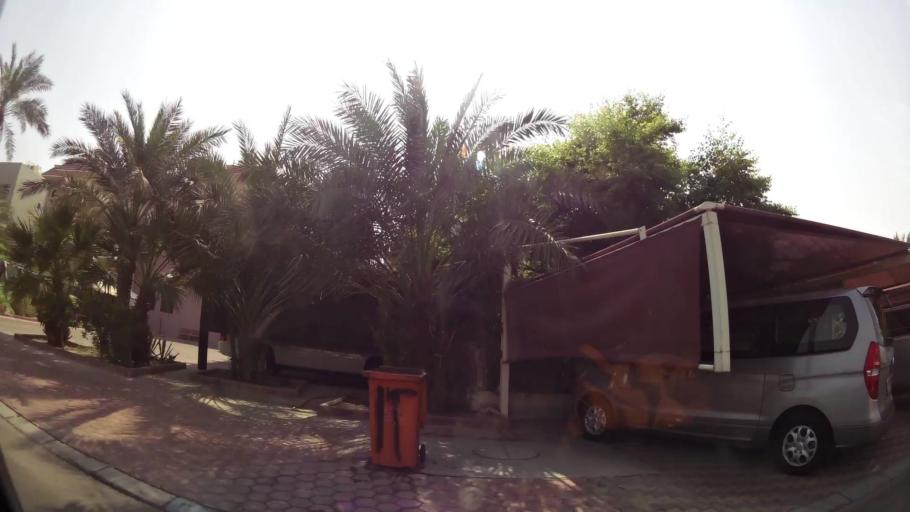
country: KW
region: Al Asimah
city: Ad Dasmah
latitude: 29.3569
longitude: 48.0090
